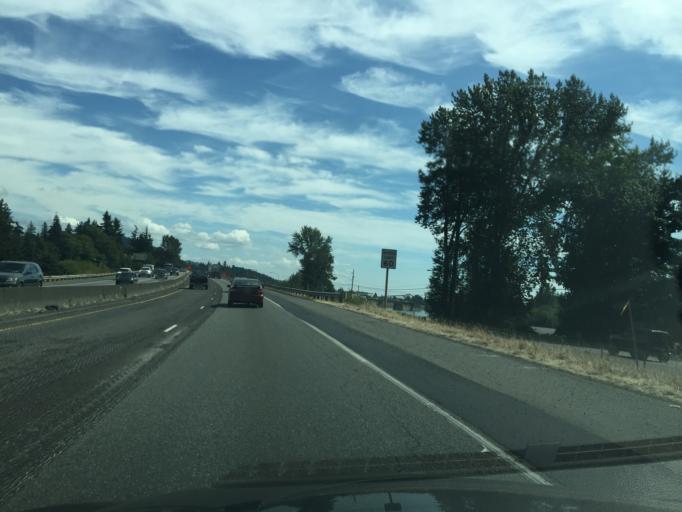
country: US
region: Washington
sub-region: Skagit County
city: Mount Vernon
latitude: 48.4289
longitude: -122.3406
